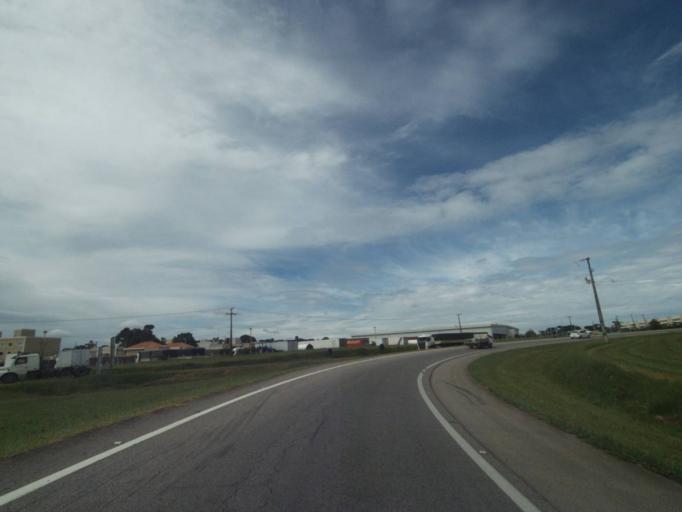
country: BR
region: Parana
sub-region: Sao Jose Dos Pinhais
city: Sao Jose dos Pinhais
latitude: -25.5130
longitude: -49.1270
